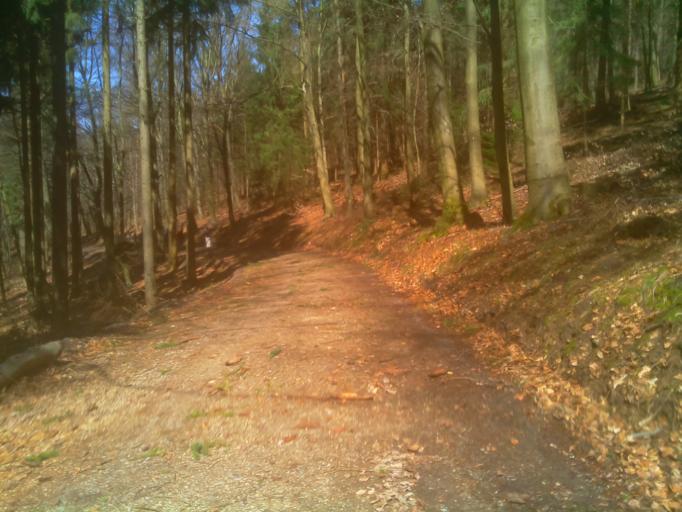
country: DE
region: Baden-Wuerttemberg
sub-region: Karlsruhe Region
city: Wilhelmsfeld
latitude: 49.4785
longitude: 8.7586
